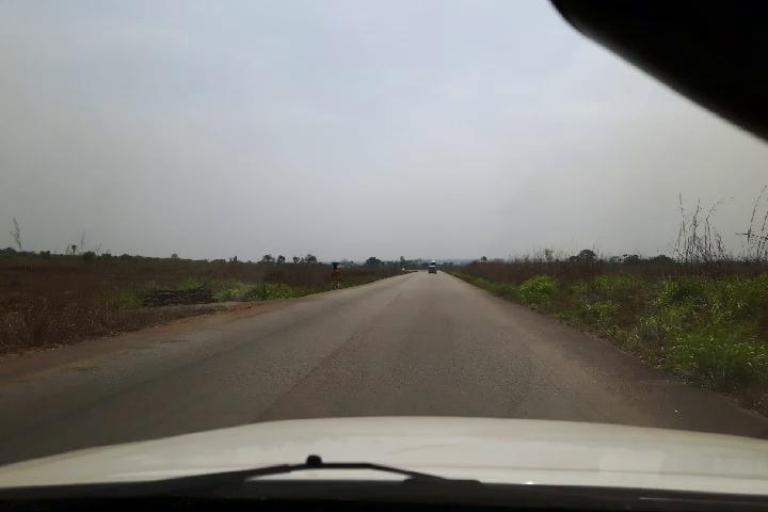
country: SL
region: Northern Province
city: Yonibana
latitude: 8.3794
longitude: -12.2025
